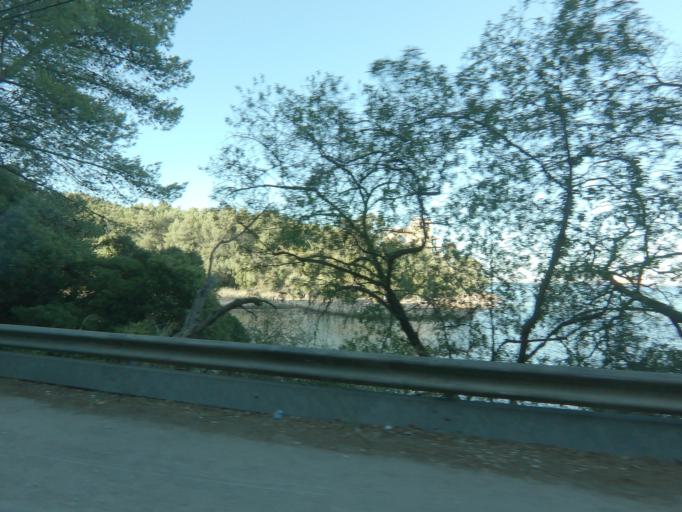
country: PT
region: Setubal
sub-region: Setubal
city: Setubal
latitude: 38.5065
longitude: -8.9267
